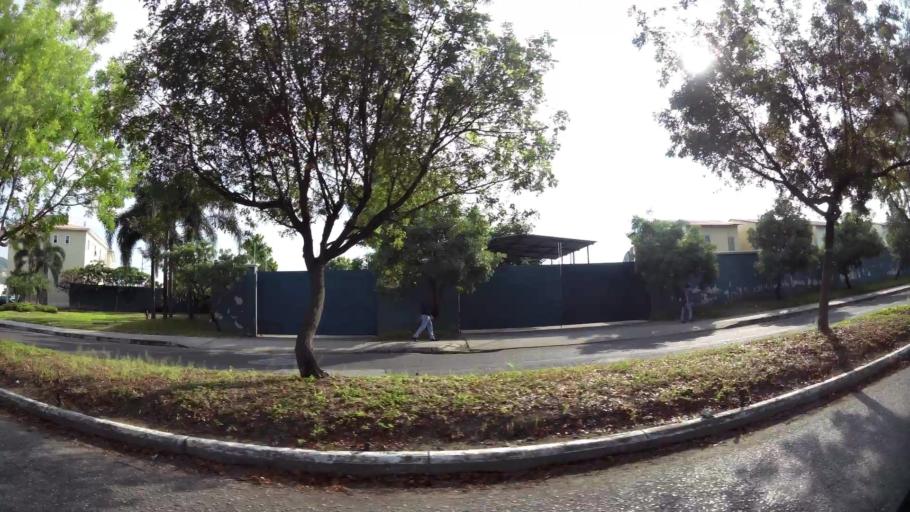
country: EC
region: Guayas
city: Eloy Alfaro
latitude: -2.0652
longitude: -79.9141
